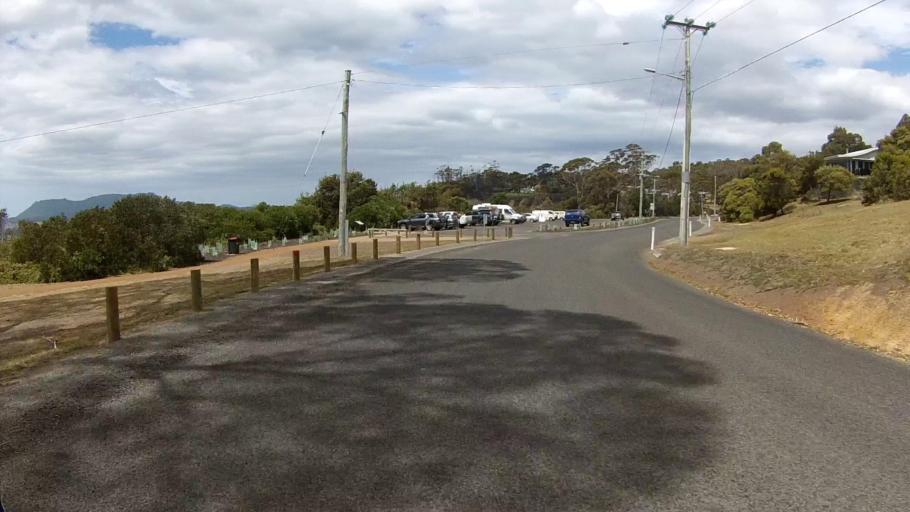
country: AU
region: Tasmania
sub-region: Sorell
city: Sorell
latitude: -42.5791
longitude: 147.9090
